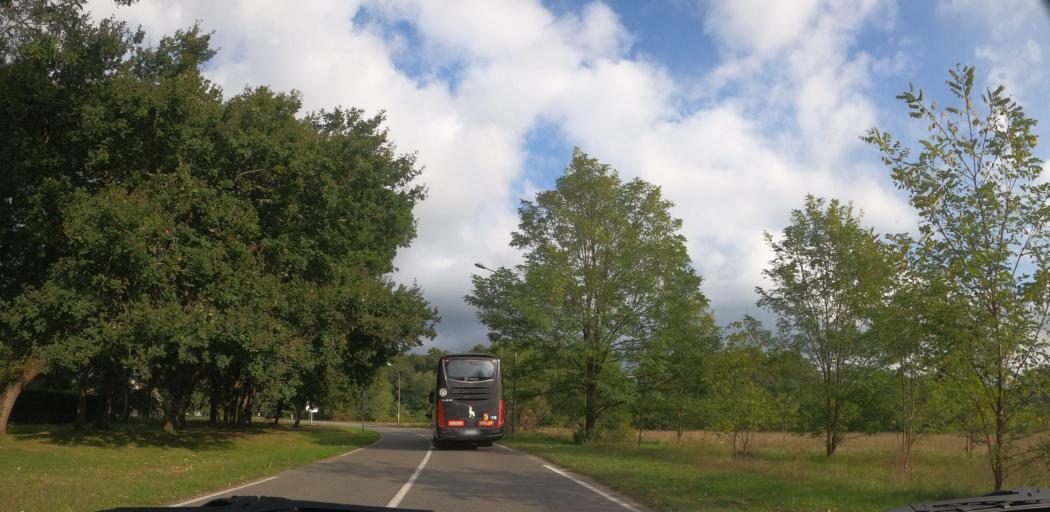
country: FR
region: Aquitaine
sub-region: Departement des Landes
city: Soustons
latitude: 43.7488
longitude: -1.3196
